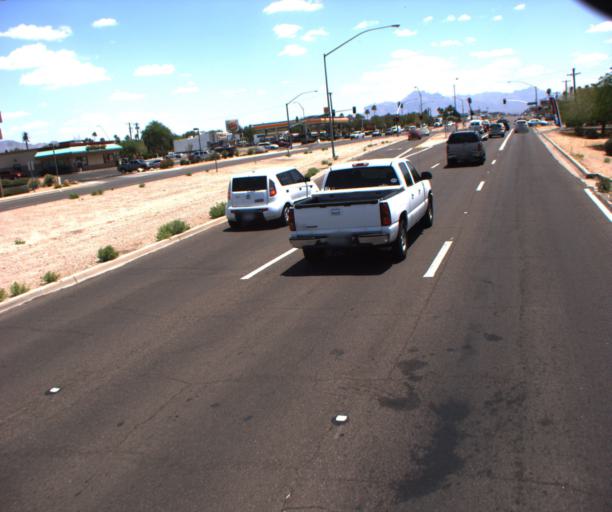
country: US
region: Arizona
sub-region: Pinal County
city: Apache Junction
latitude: 33.4151
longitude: -111.6342
